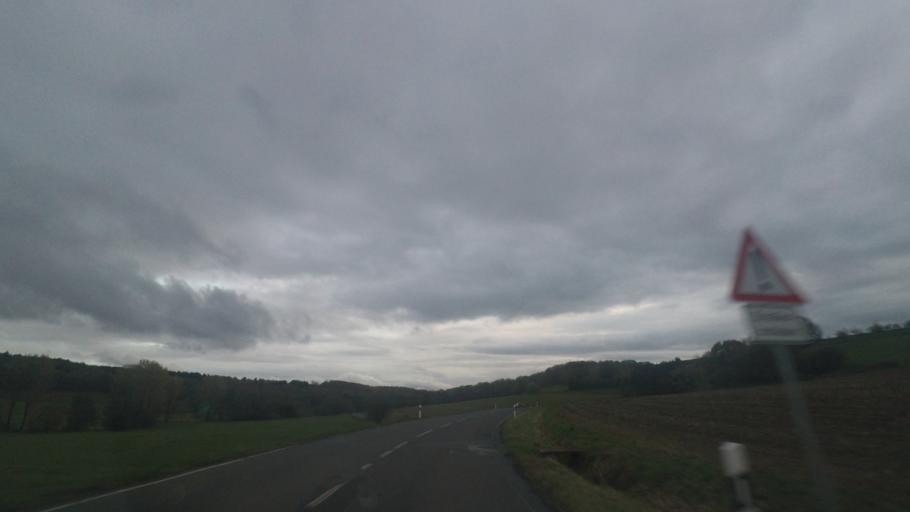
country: DE
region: Hesse
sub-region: Regierungsbezirk Darmstadt
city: Steinau an der Strasse
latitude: 50.3525
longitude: 9.4303
